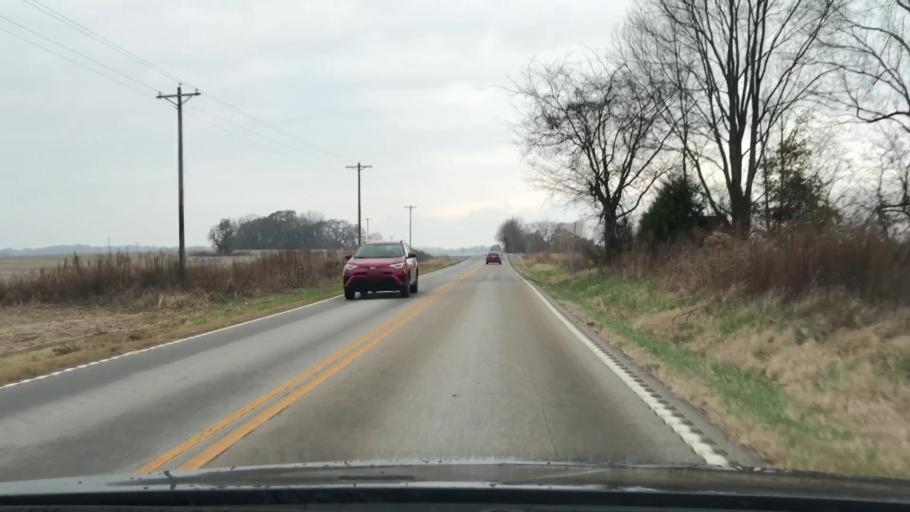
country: US
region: Kentucky
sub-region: Simpson County
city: Franklin
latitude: 36.7080
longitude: -86.4573
